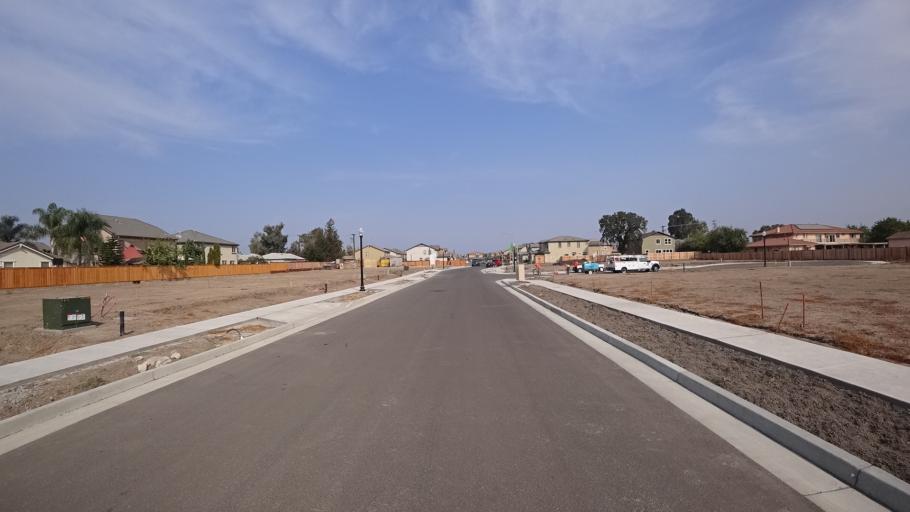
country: US
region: California
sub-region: Sacramento County
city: Laguna
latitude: 38.4494
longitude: -121.4129
